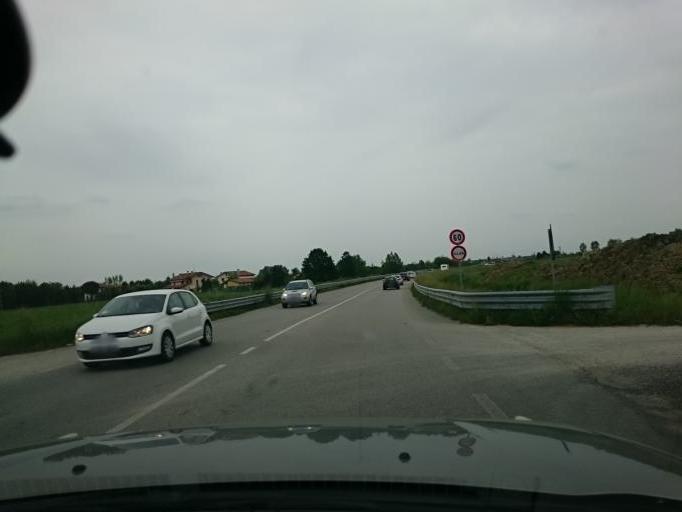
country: IT
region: Veneto
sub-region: Provincia di Padova
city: Montegrotto Terme
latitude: 45.3193
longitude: 11.7964
